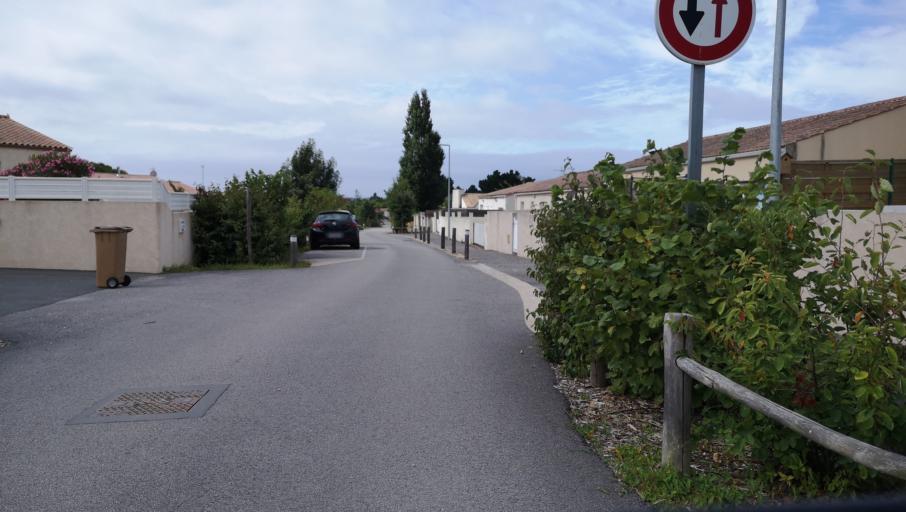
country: FR
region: Pays de la Loire
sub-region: Departement de la Vendee
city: Vaire
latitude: 46.5827
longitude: -1.7967
